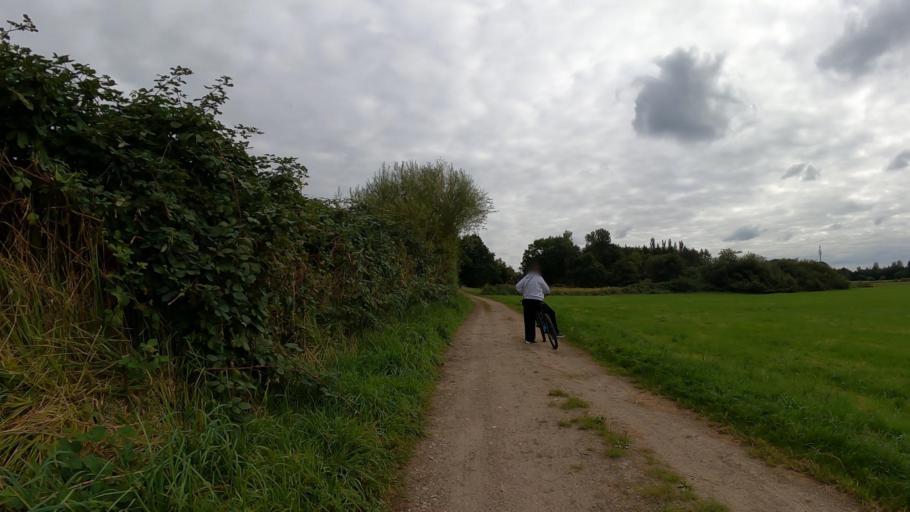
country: DE
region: Schleswig-Holstein
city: Bornsen
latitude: 53.4662
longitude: 10.2862
